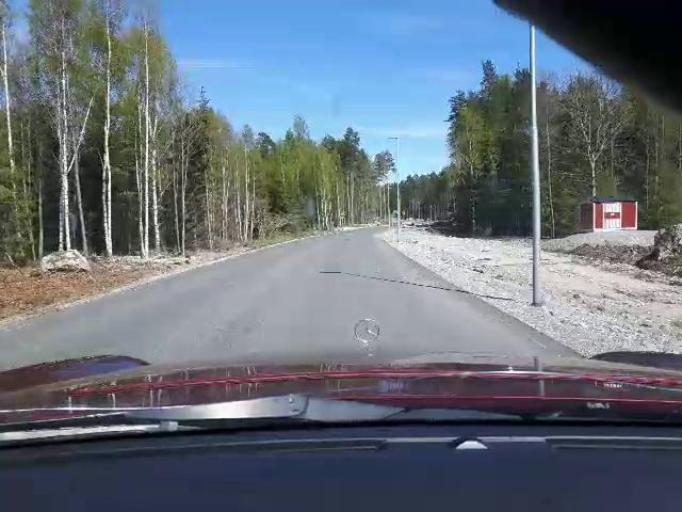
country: SE
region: OErebro
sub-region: Orebro Kommun
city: Orebro
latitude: 59.3030
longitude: 15.2453
